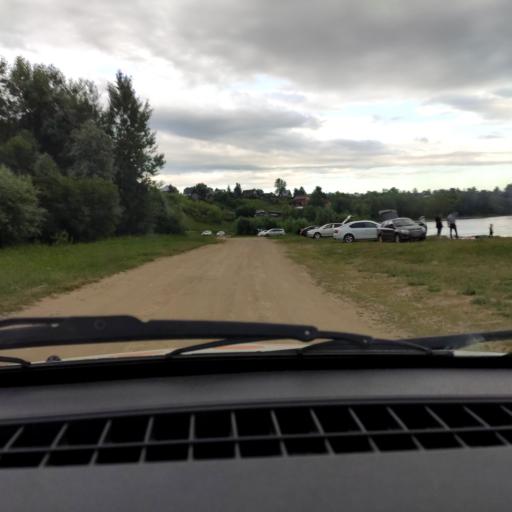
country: RU
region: Bashkortostan
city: Iglino
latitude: 54.7965
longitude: 56.2312
